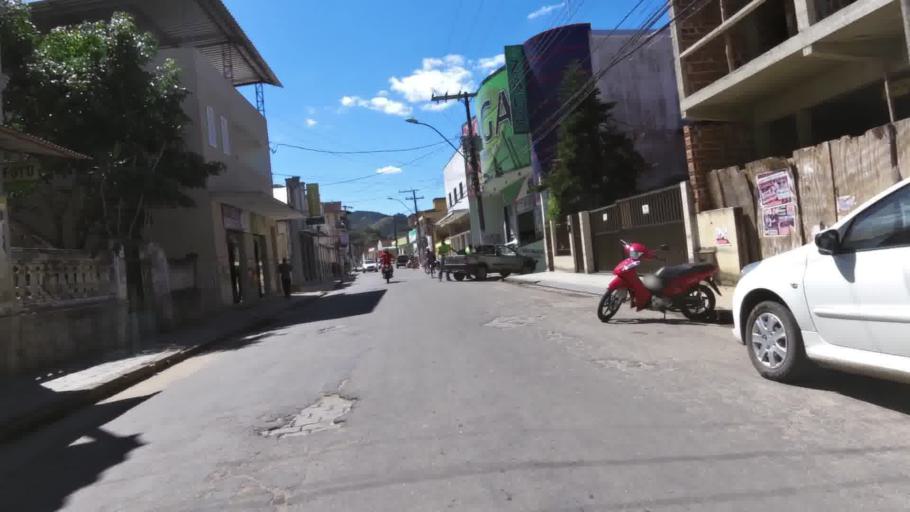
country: BR
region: Espirito Santo
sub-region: Rio Novo Do Sul
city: Rio Novo do Sul
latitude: -20.8625
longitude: -40.9353
